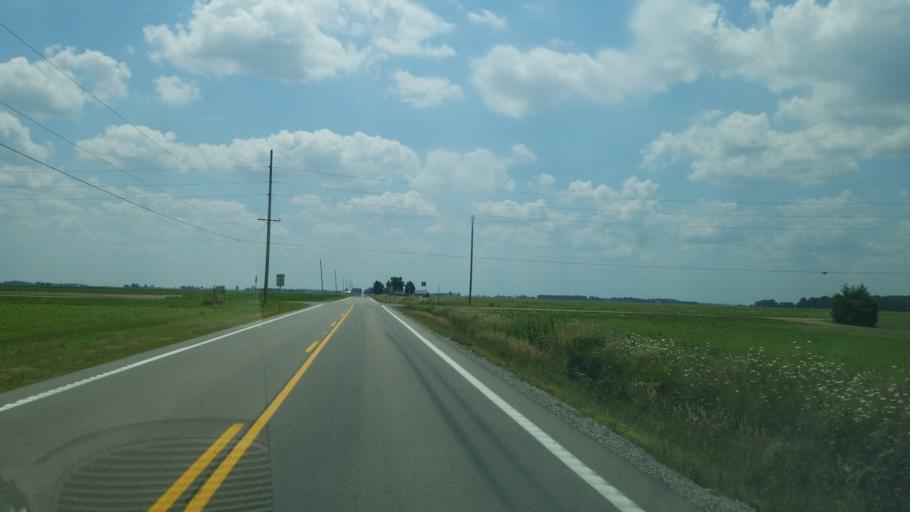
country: US
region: Ohio
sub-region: Henry County
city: Deshler
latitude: 41.3280
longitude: -83.9415
